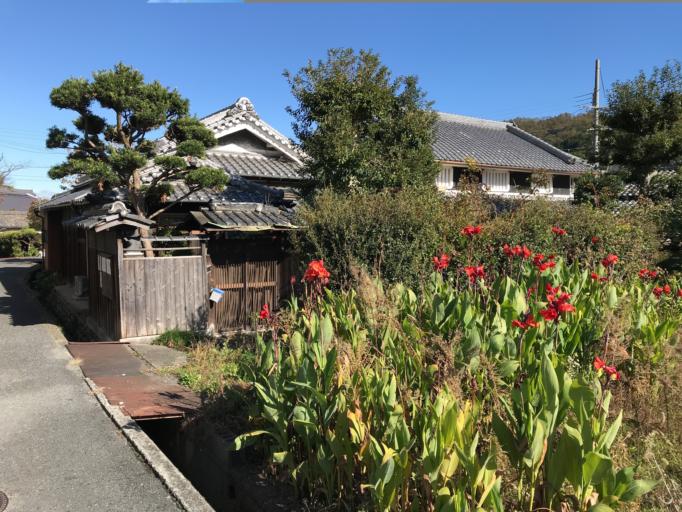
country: JP
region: Osaka
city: Tondabayashicho
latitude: 34.4572
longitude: 135.5765
